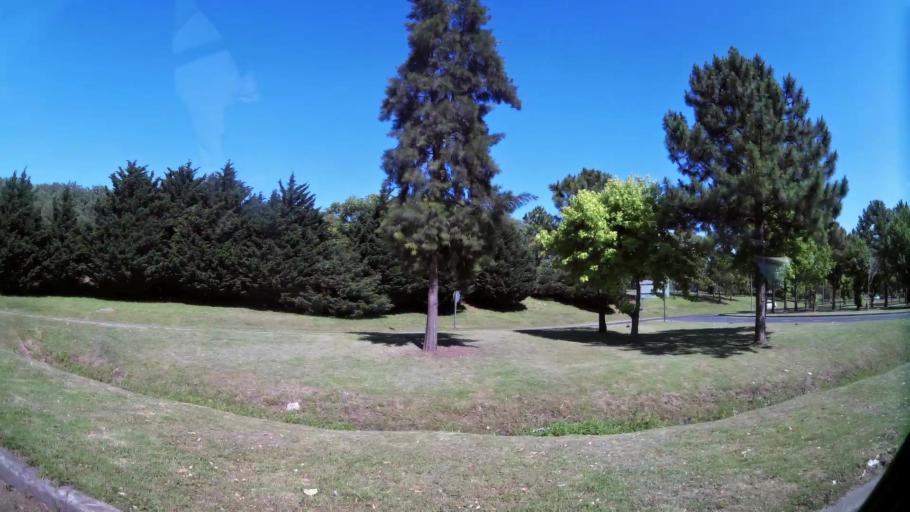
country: AR
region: Buenos Aires
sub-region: Partido de San Isidro
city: San Isidro
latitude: -34.4906
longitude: -58.5574
